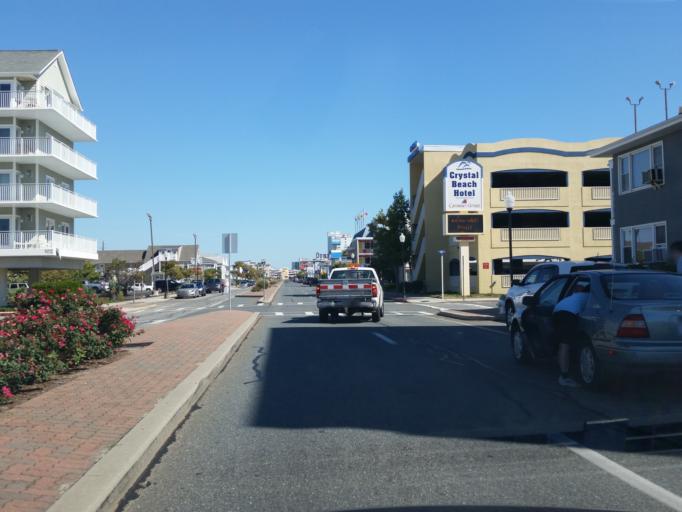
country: US
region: Maryland
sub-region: Worcester County
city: Ocean City
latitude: 38.3537
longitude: -75.0753
